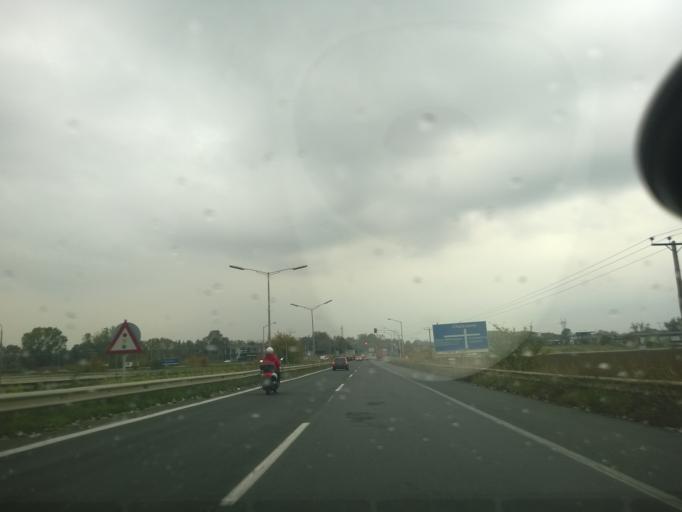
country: GR
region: Central Macedonia
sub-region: Nomos Thessalonikis
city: Gefyra
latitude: 40.7222
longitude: 22.6976
